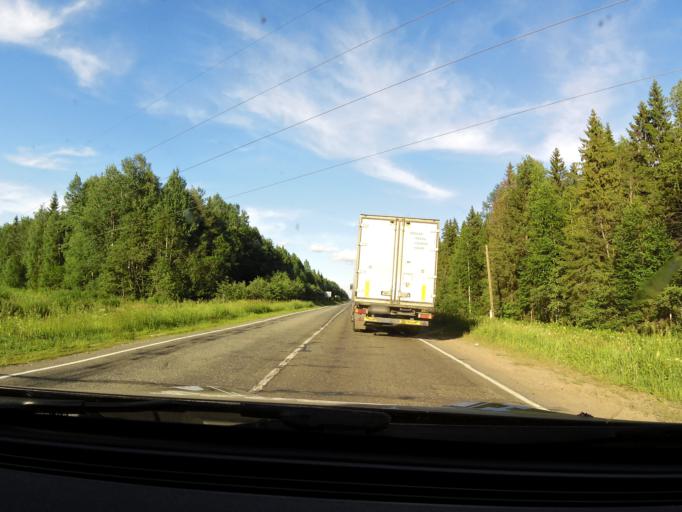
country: RU
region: Kirov
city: Belorechensk
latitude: 58.8009
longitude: 52.4130
